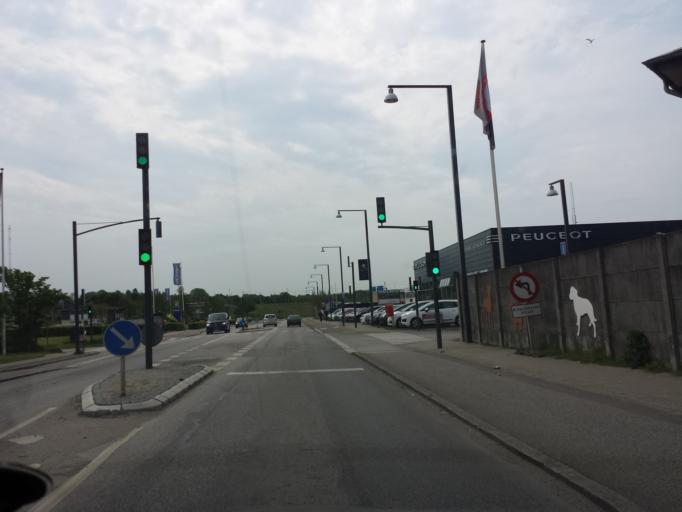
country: DK
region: Capital Region
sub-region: Rodovre Kommune
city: Rodovre
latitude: 55.6939
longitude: 12.4327
